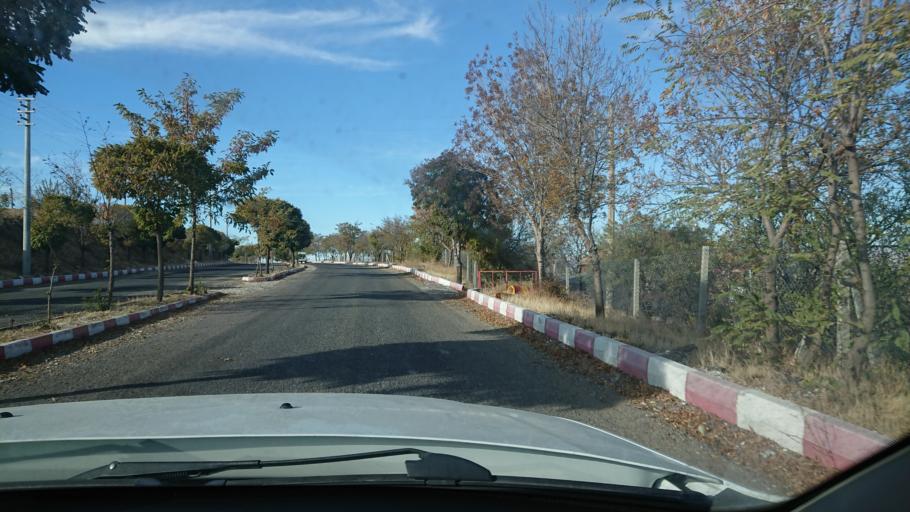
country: TR
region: Aksaray
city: Sariyahsi
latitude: 38.9652
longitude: 33.8750
